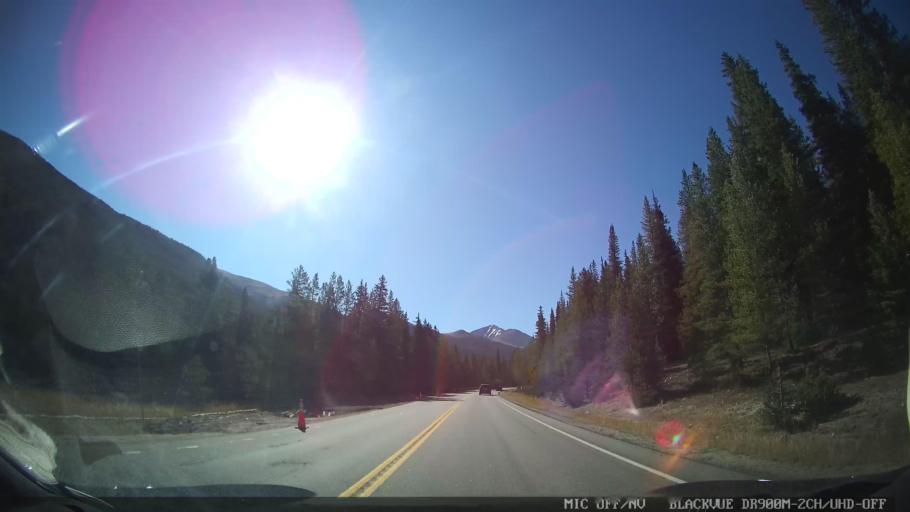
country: US
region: Colorado
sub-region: Summit County
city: Frisco
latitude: 39.4876
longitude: -106.1338
